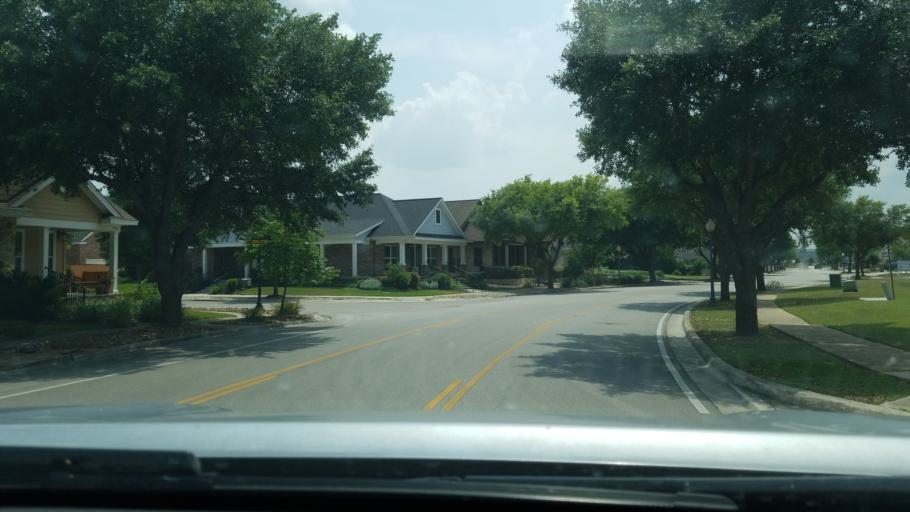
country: US
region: Texas
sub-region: Comal County
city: New Braunfels
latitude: 29.7276
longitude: -98.1008
